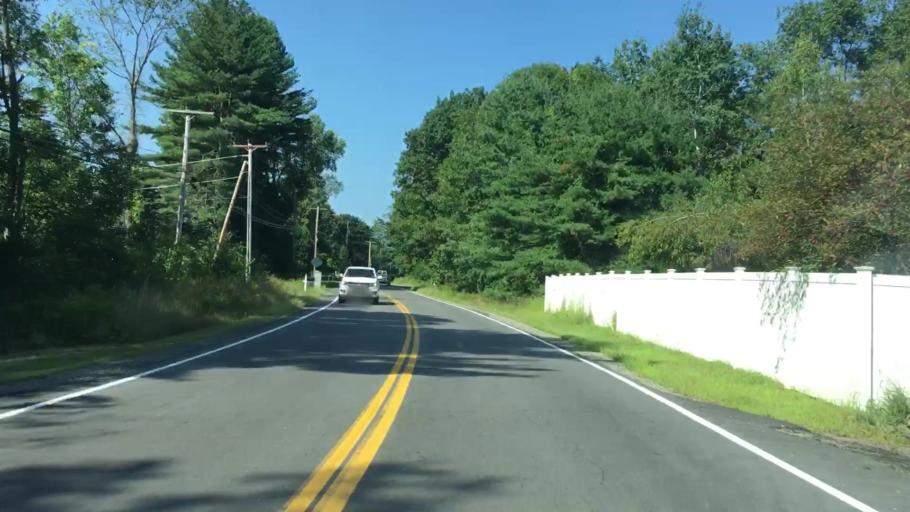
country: US
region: New Hampshire
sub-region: Rockingham County
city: East Kingston
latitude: 42.9301
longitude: -71.0283
